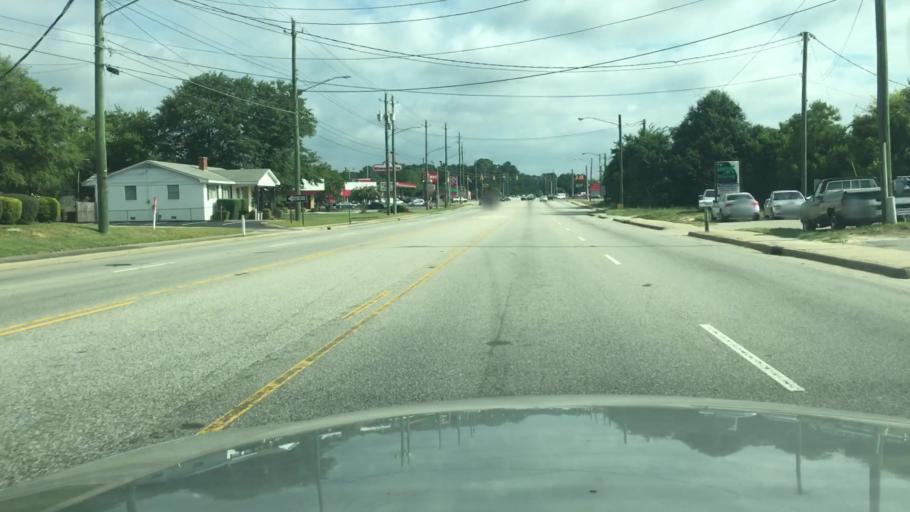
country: US
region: North Carolina
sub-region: Cumberland County
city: Hope Mills
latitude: 35.0029
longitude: -78.9672
